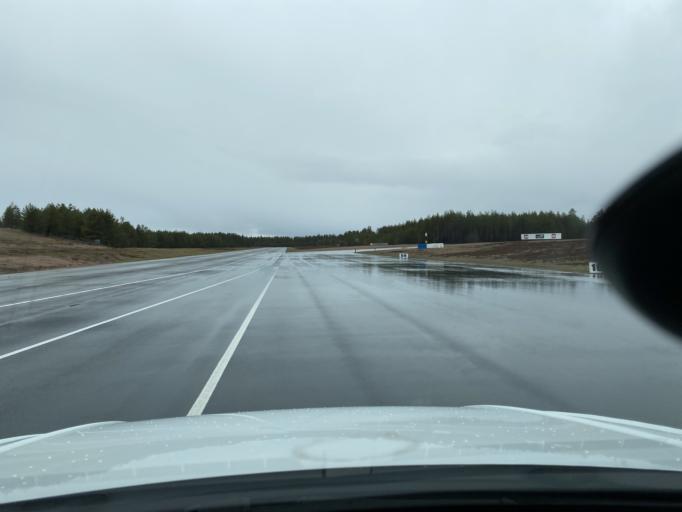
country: FI
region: Satakunta
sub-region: Pori
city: Vampula
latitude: 60.9776
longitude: 22.6577
